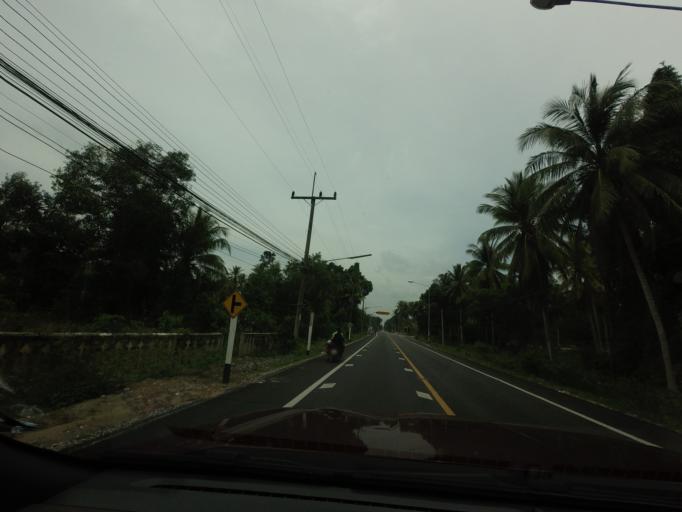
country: TH
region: Pattani
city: Yaring
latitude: 6.8592
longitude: 101.3642
